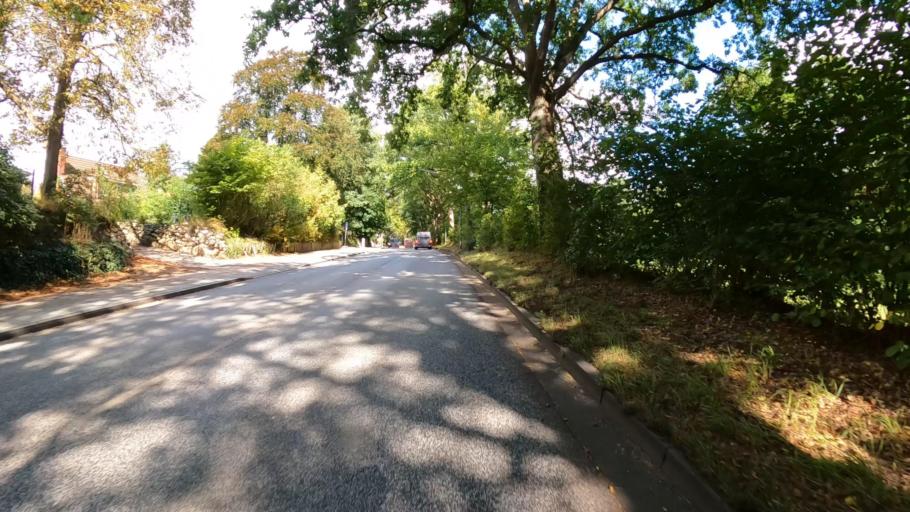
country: DE
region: Hamburg
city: Lemsahl-Mellingstedt
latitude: 53.6842
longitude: 10.0953
